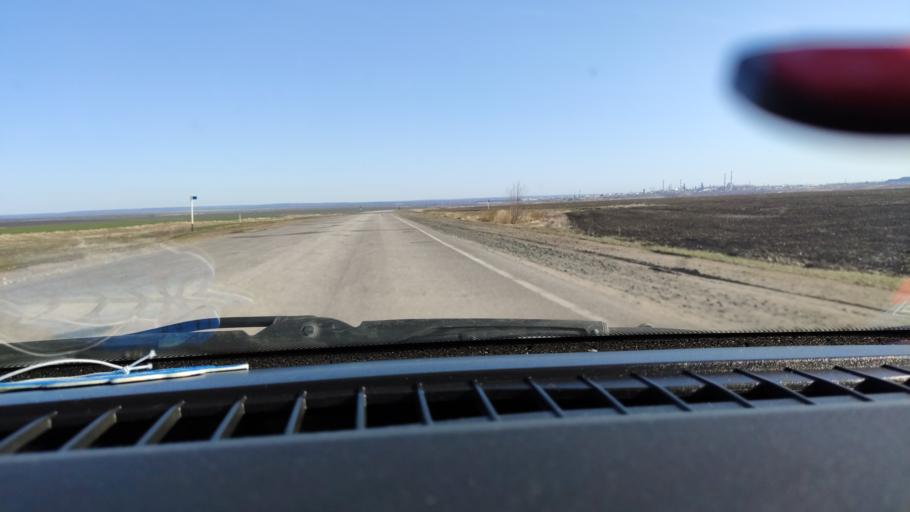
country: RU
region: Samara
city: Varlamovo
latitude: 53.0300
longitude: 48.3346
